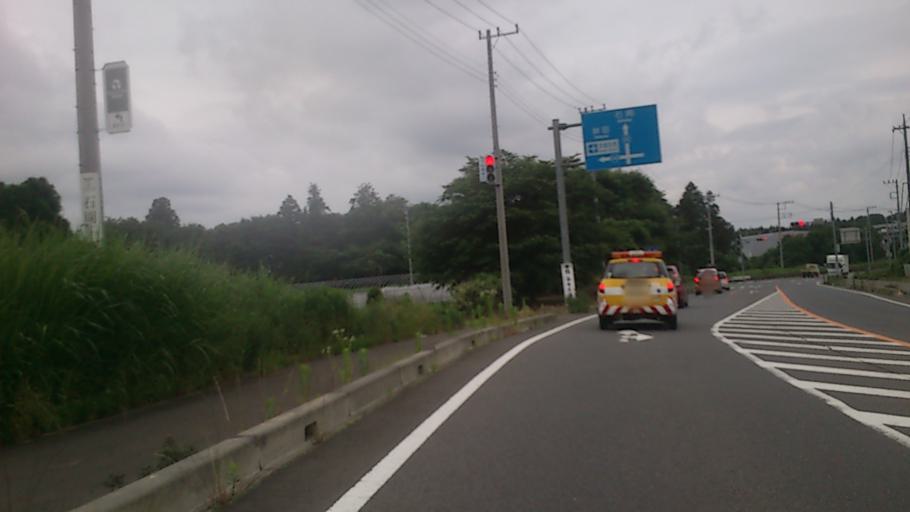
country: JP
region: Ibaraki
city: Ishioka
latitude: 36.2362
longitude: 140.3164
